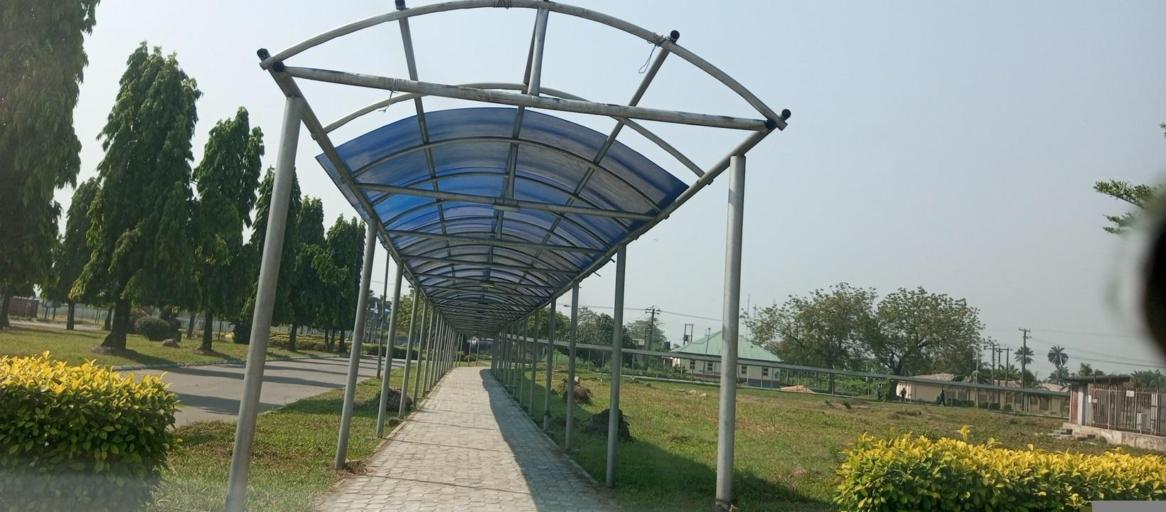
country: NG
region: Rivers
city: Emuoha
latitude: 4.9036
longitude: 6.9208
